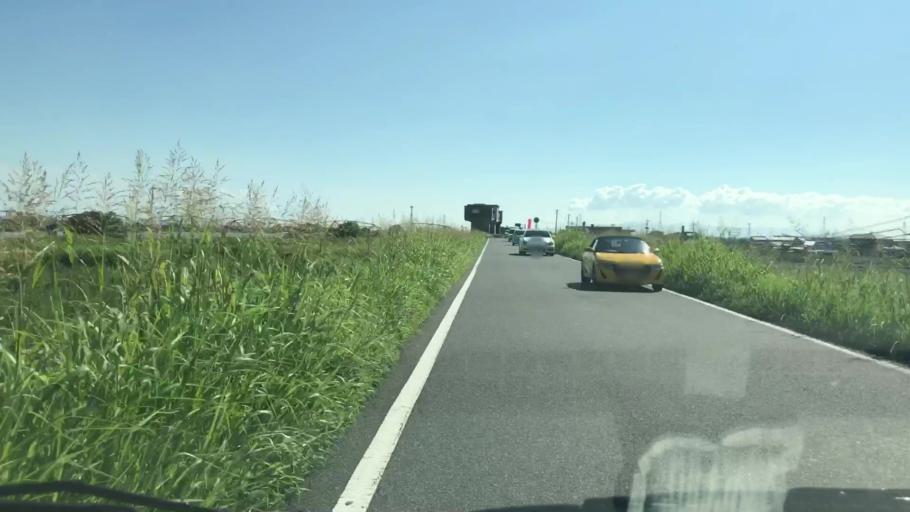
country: JP
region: Saga Prefecture
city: Kanzakimachi-kanzaki
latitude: 33.2657
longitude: 130.4200
